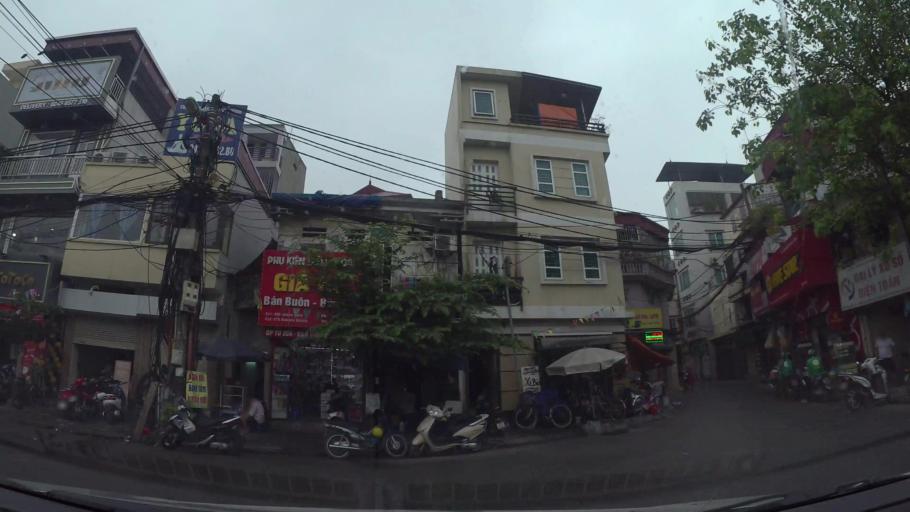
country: VN
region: Ha Noi
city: Cau Giay
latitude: 21.0238
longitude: 105.7976
